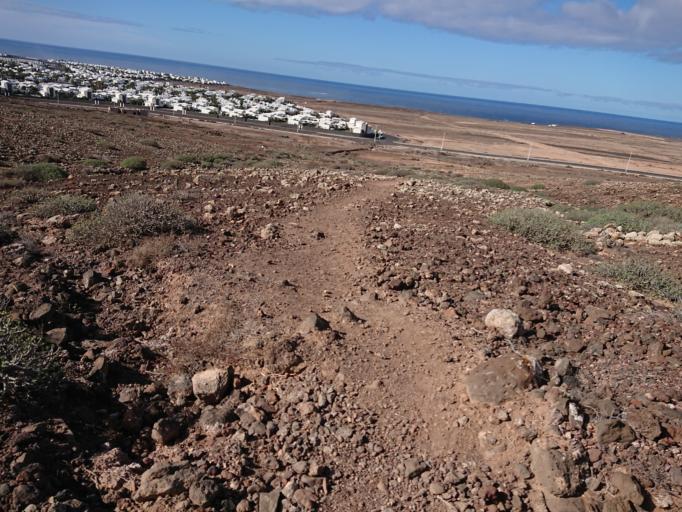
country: ES
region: Canary Islands
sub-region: Provincia de Las Palmas
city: Playa Blanca
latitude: 28.8723
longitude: -13.8607
